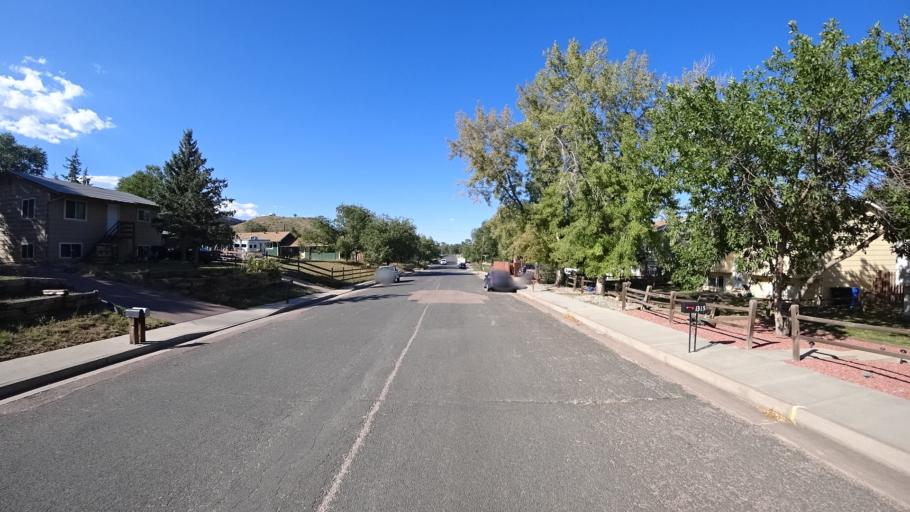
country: US
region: Colorado
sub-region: El Paso County
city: Colorado Springs
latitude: 38.8365
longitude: -104.8716
